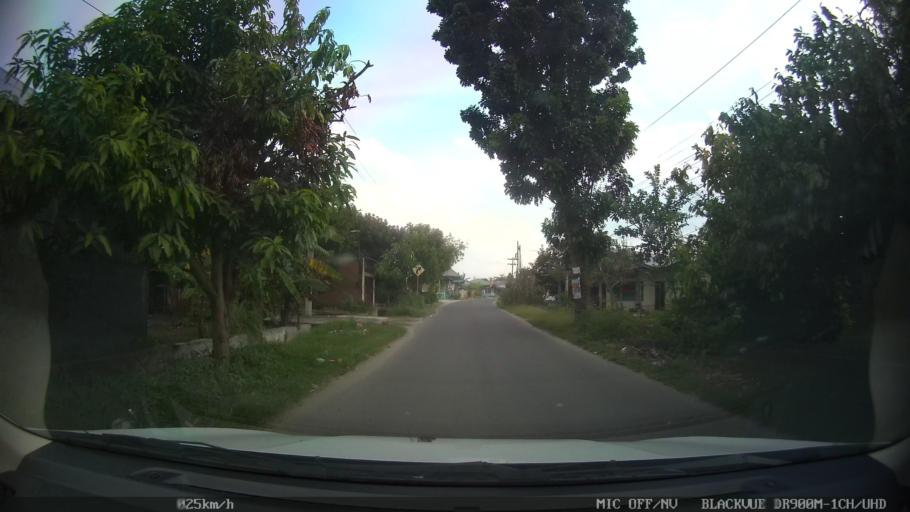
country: ID
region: North Sumatra
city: Binjai
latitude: 3.6440
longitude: 98.4975
